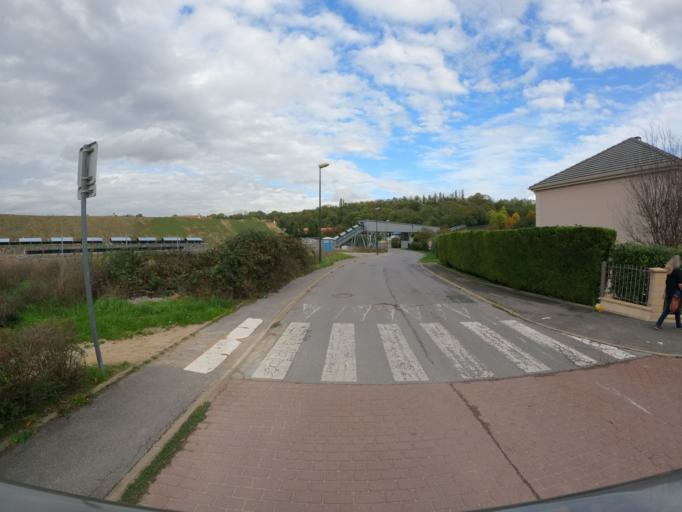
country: FR
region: Ile-de-France
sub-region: Departement de Seine-Saint-Denis
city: Montfermeil
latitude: 48.8905
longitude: 2.5791
